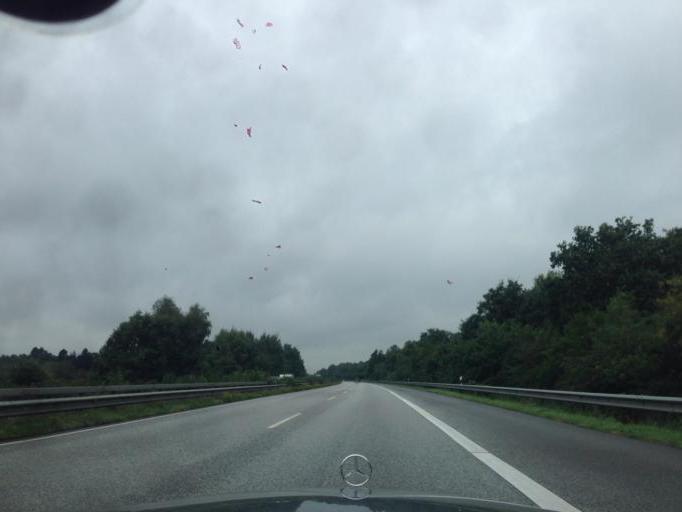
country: DE
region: Schleswig-Holstein
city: Datgen
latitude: 54.1904
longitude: 9.9240
